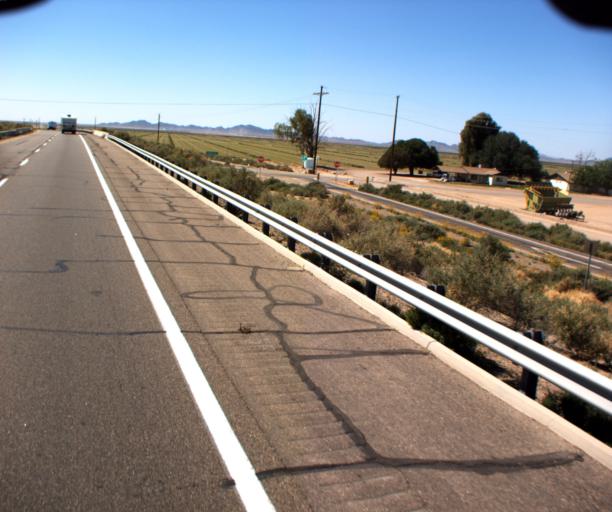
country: US
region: Arizona
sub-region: Maricopa County
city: Gila Bend
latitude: 32.9221
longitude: -112.8867
